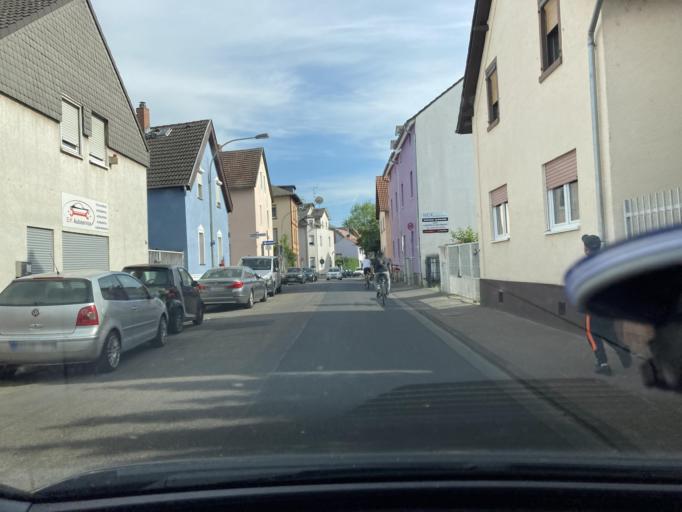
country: DE
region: Hesse
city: Niederrad
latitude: 50.0921
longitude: 8.6003
